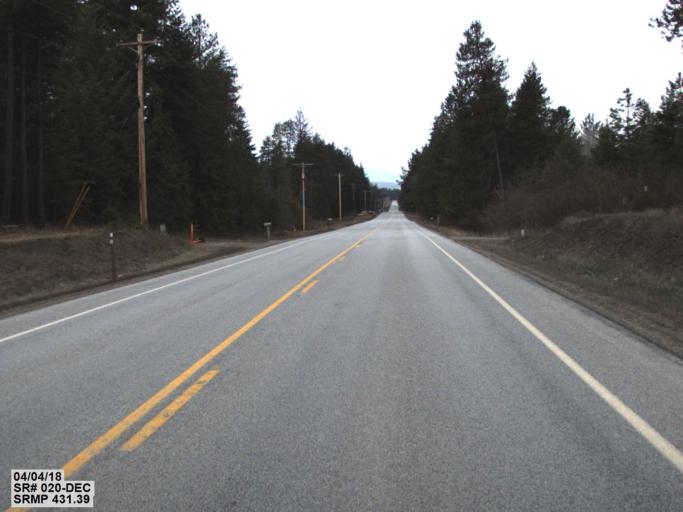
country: US
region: Washington
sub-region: Pend Oreille County
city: Newport
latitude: 48.2256
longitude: -117.1328
